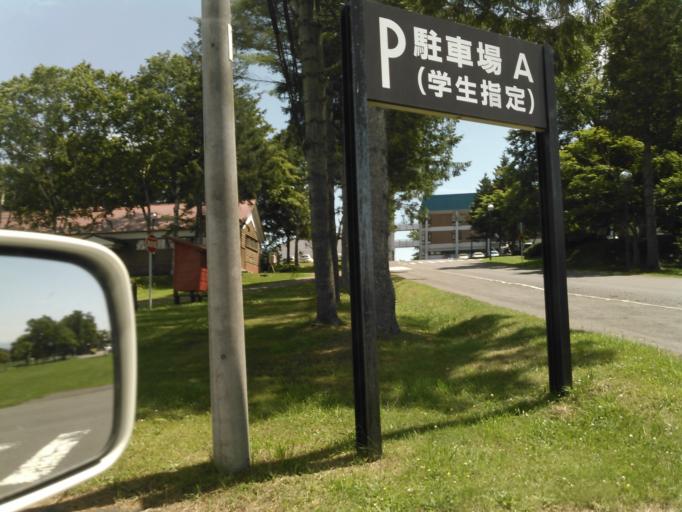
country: JP
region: Hokkaido
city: Ebetsu
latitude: 43.0750
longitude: 141.5111
